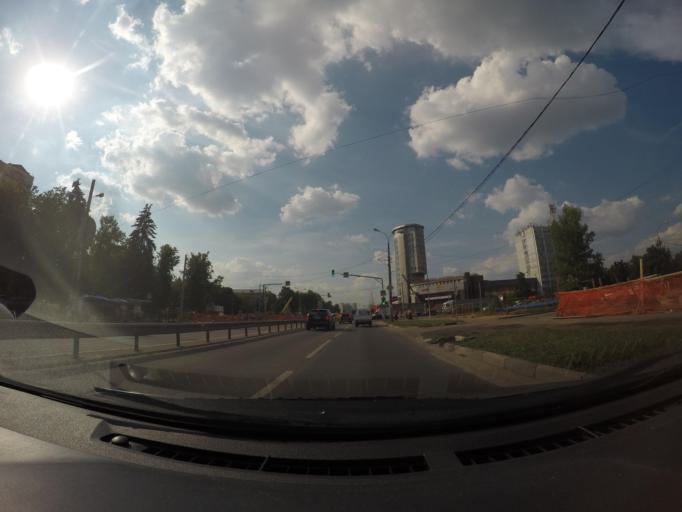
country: RU
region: Moskovskaya
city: Lyubertsy
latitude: 55.6803
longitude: 37.8898
